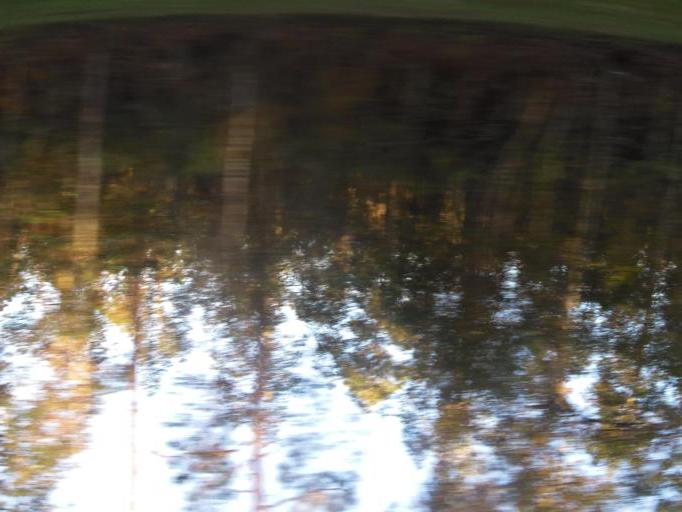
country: US
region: Florida
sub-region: Clay County
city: Green Cove Springs
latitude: 29.8921
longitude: -81.5692
